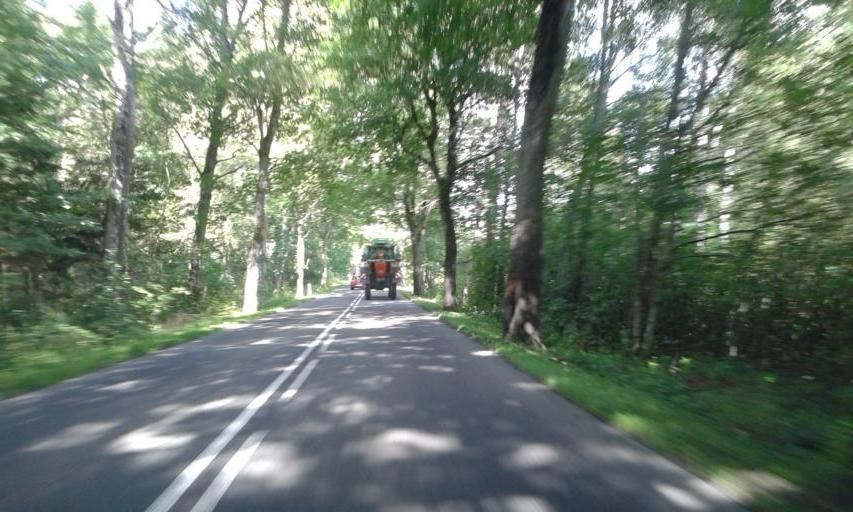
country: PL
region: West Pomeranian Voivodeship
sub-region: Powiat slawienski
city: Slawno
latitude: 54.2435
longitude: 16.7076
